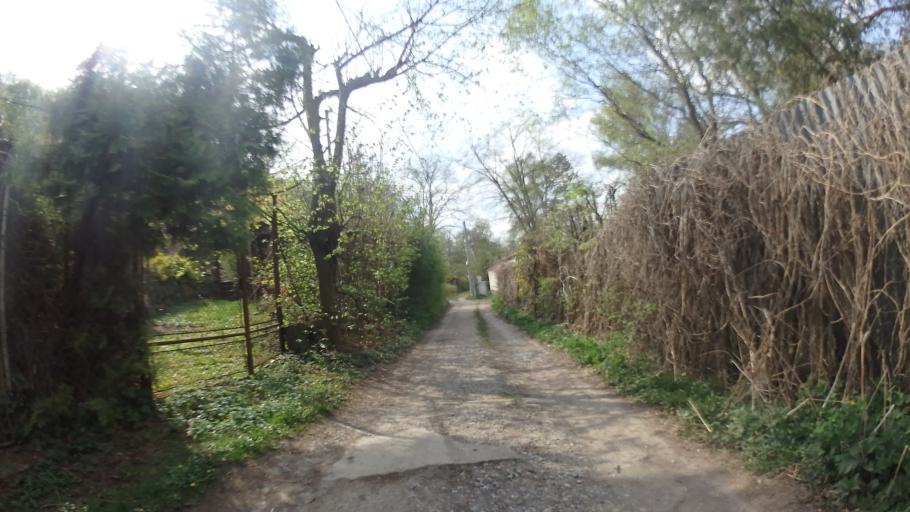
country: CZ
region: South Moravian
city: Ostopovice
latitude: 49.2174
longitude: 16.5489
